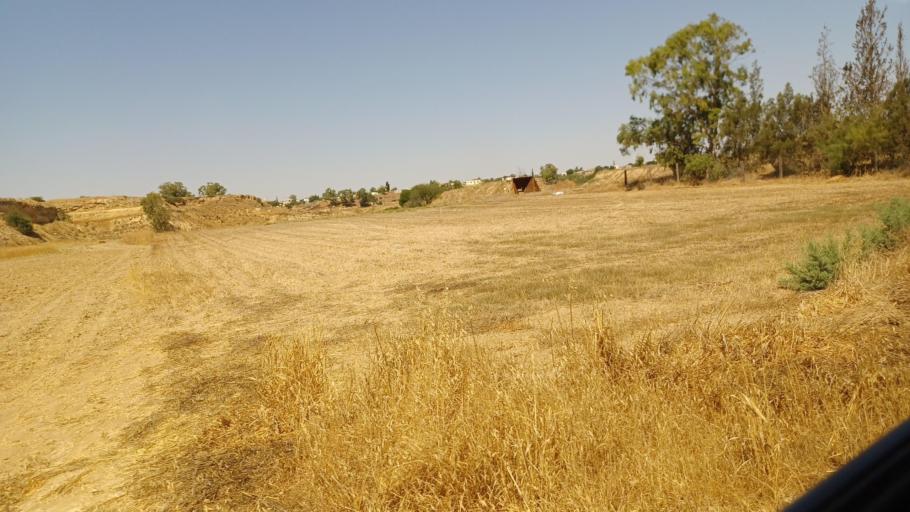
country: CY
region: Ammochostos
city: Acheritou
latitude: 35.1023
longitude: 33.8724
